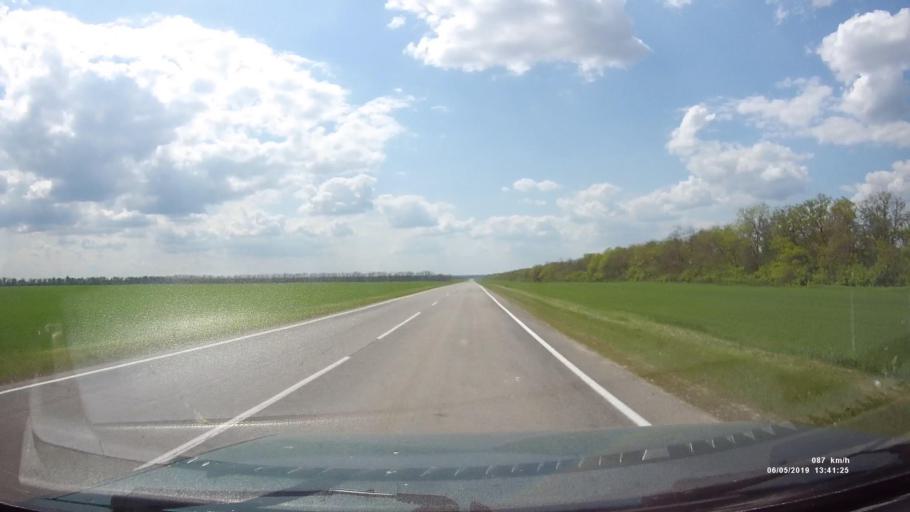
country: RU
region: Rostov
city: Ust'-Donetskiy
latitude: 47.6628
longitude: 40.6762
